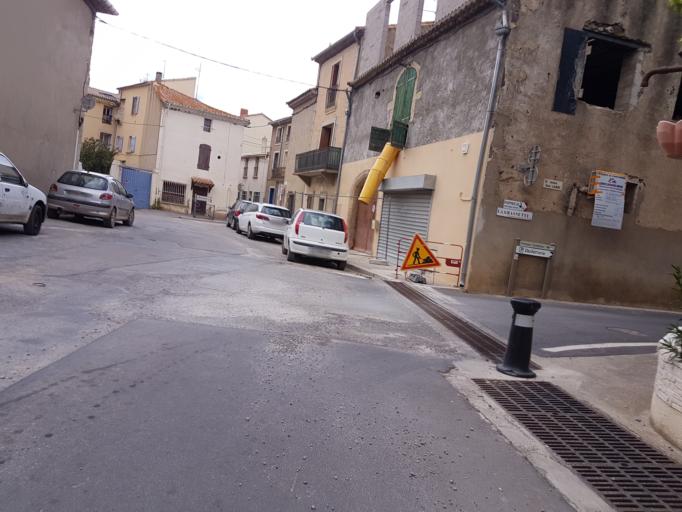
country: FR
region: Languedoc-Roussillon
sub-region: Departement de l'Herault
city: Cers
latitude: 43.3229
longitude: 3.3056
